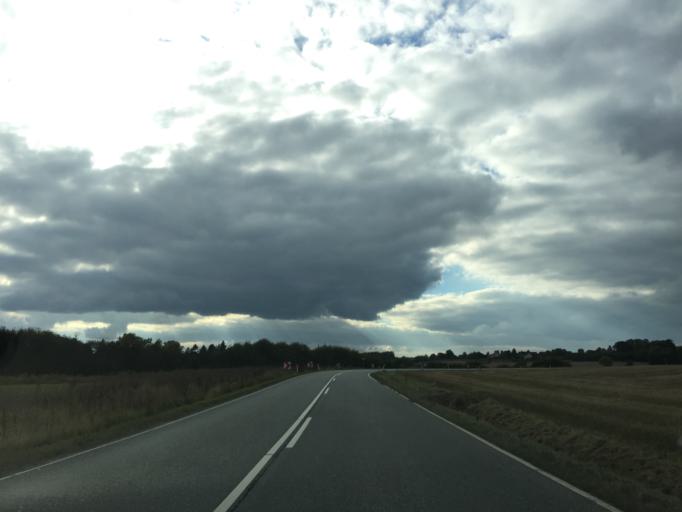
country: DK
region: Central Jutland
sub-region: Randers Kommune
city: Langa
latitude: 56.3458
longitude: 9.8859
